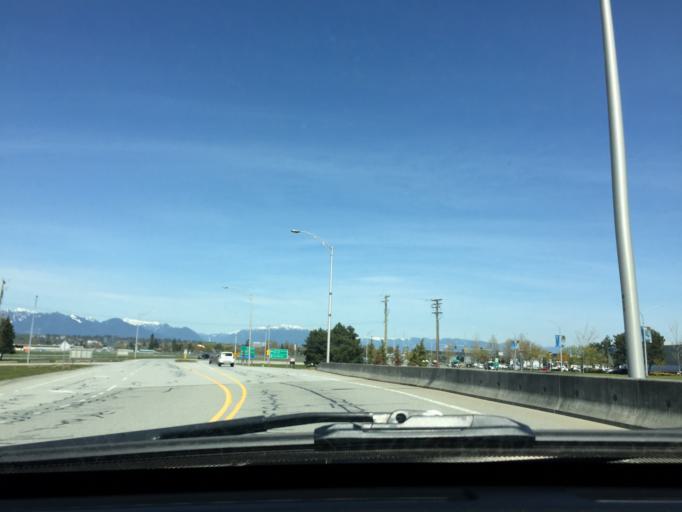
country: CA
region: British Columbia
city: Richmond
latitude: 49.1784
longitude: -123.1558
